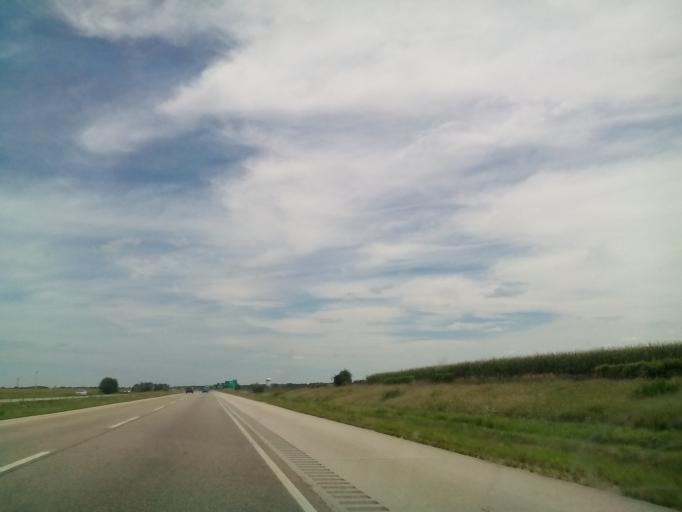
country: US
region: Illinois
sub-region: DeKalb County
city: DeKalb
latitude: 41.9001
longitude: -88.8038
